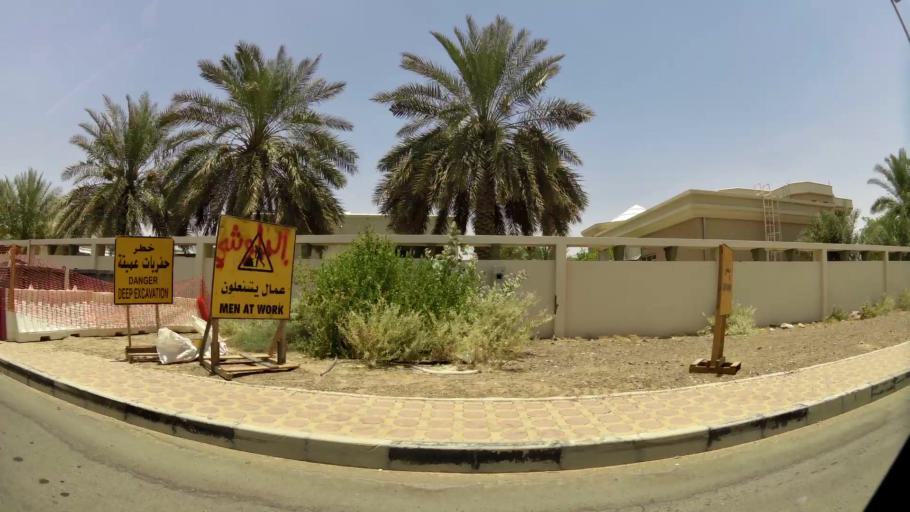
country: OM
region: Al Buraimi
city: Al Buraymi
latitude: 24.2681
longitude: 55.7295
